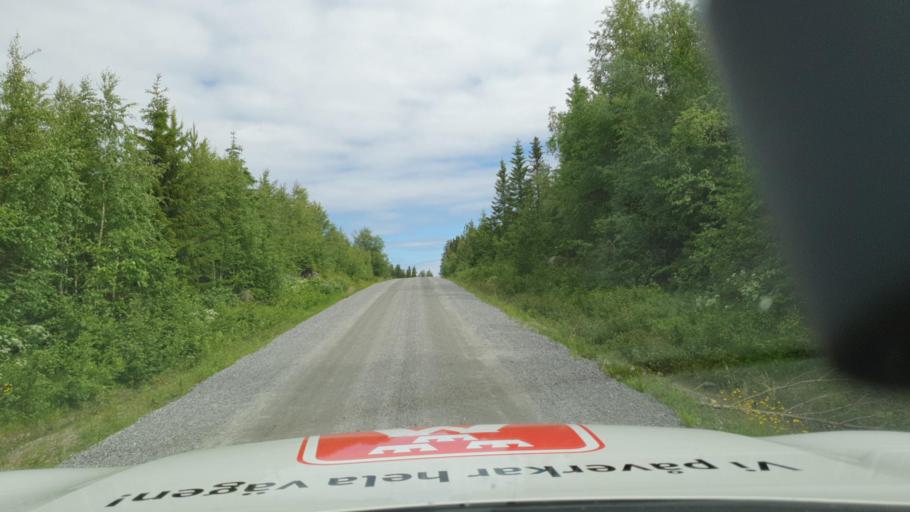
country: SE
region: Vaesterbotten
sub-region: Skelleftea Kommun
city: Langsele
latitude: 64.6327
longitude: 20.2556
